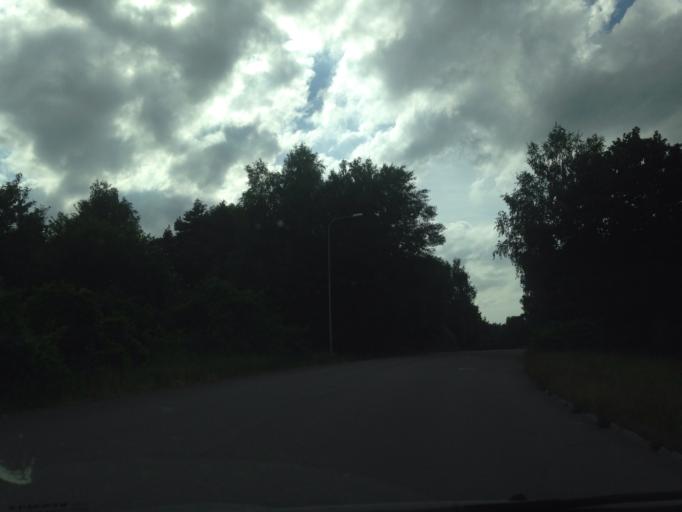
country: SE
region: Vaestra Goetaland
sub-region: Goteborg
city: Majorna
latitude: 57.7456
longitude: 11.9236
